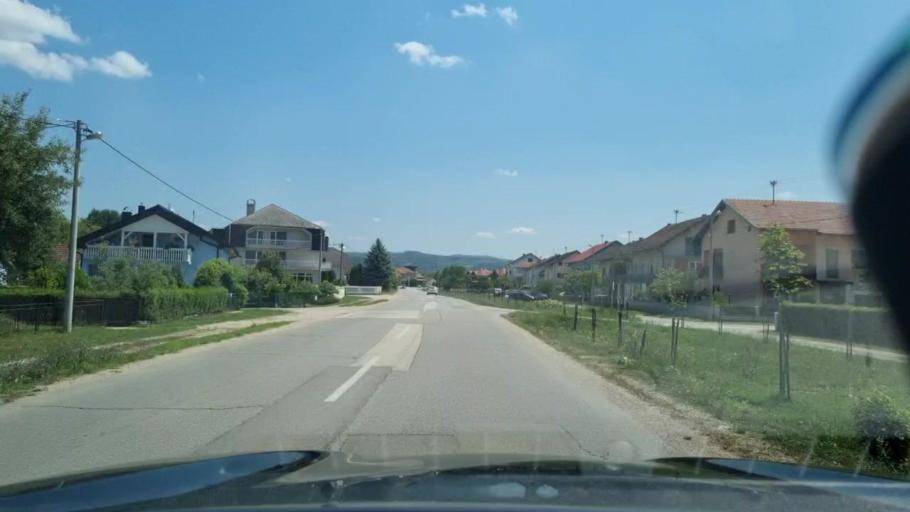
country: BA
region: Federation of Bosnia and Herzegovina
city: Sanski Most
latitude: 44.7711
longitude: 16.6628
